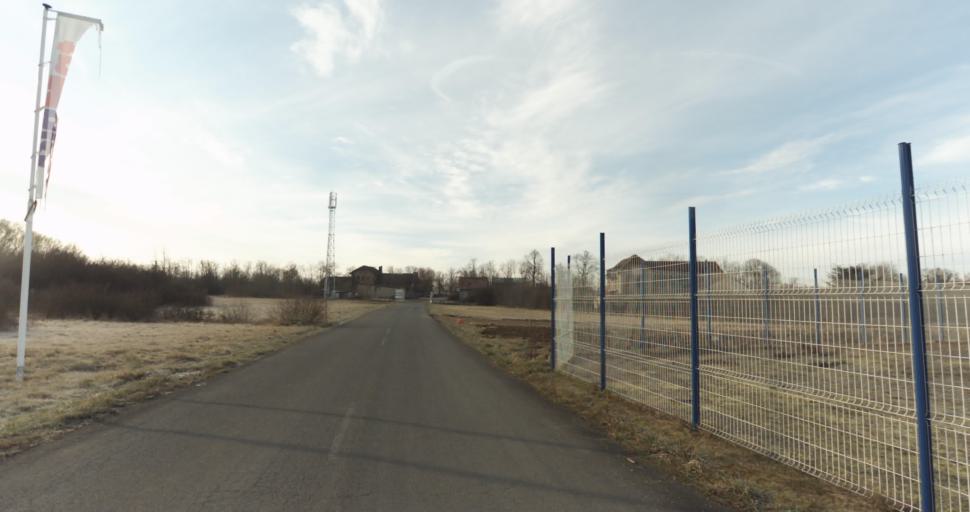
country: FR
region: Lorraine
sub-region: Departement de Meurthe-et-Moselle
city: Jarny
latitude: 49.1575
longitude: 5.8935
